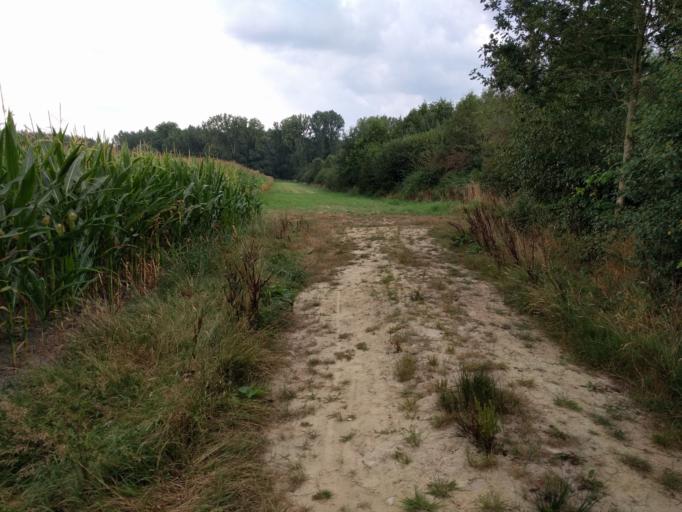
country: BE
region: Flanders
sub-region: Provincie West-Vlaanderen
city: Oostkamp
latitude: 51.1253
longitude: 3.2282
